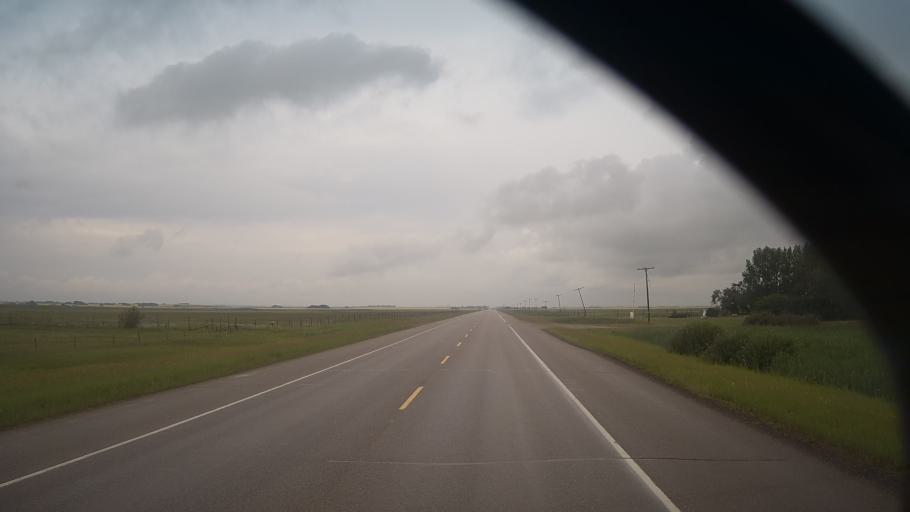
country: CA
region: Saskatchewan
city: Unity
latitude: 52.4349
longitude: -108.9762
